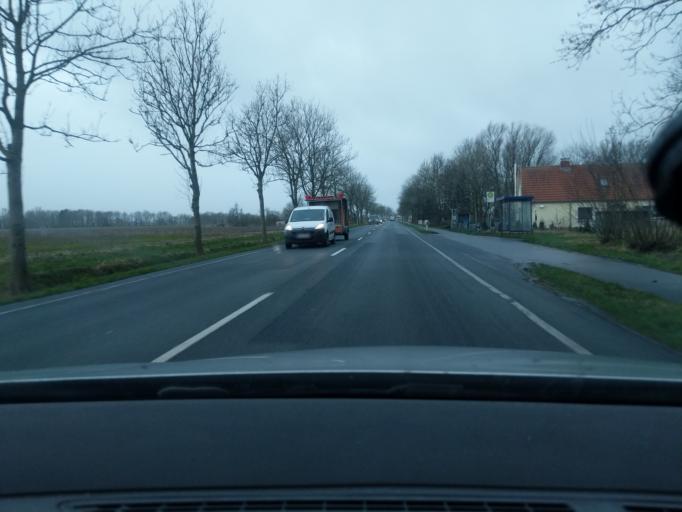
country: DE
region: Lower Saxony
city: Nordleda
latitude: 53.8061
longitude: 8.8016
